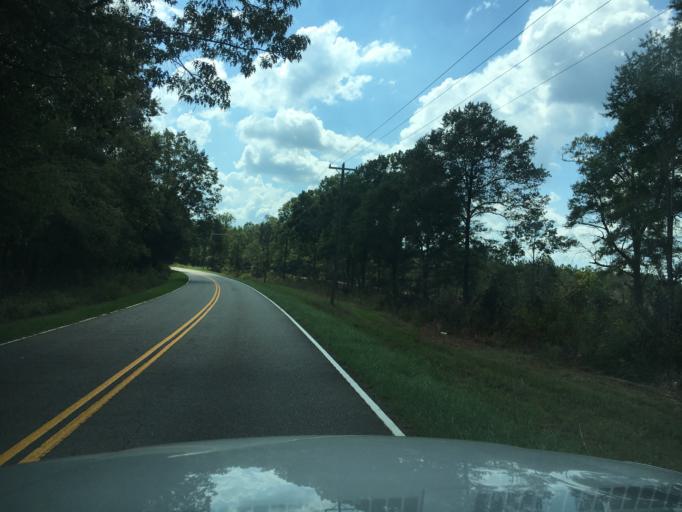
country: US
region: South Carolina
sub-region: Greenwood County
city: Greenwood
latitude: 34.0758
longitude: -82.1456
